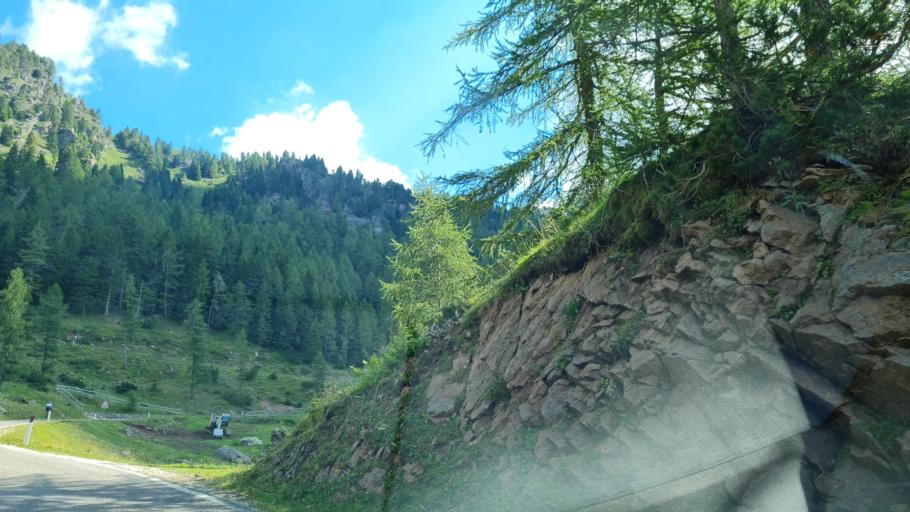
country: IT
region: Trentino-Alto Adige
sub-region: Provincia di Trento
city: Palu del Fersina
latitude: 46.1691
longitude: 11.4374
